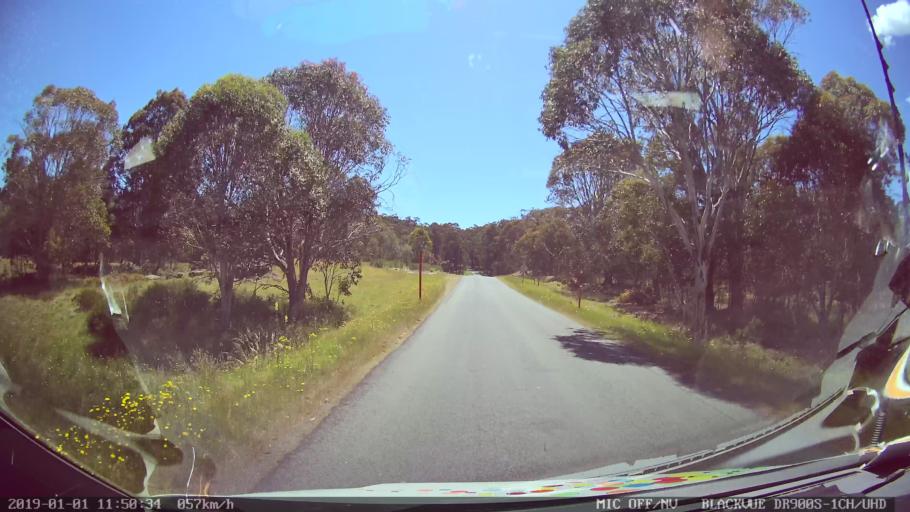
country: AU
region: New South Wales
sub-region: Snowy River
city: Jindabyne
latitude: -35.8904
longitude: 148.4221
